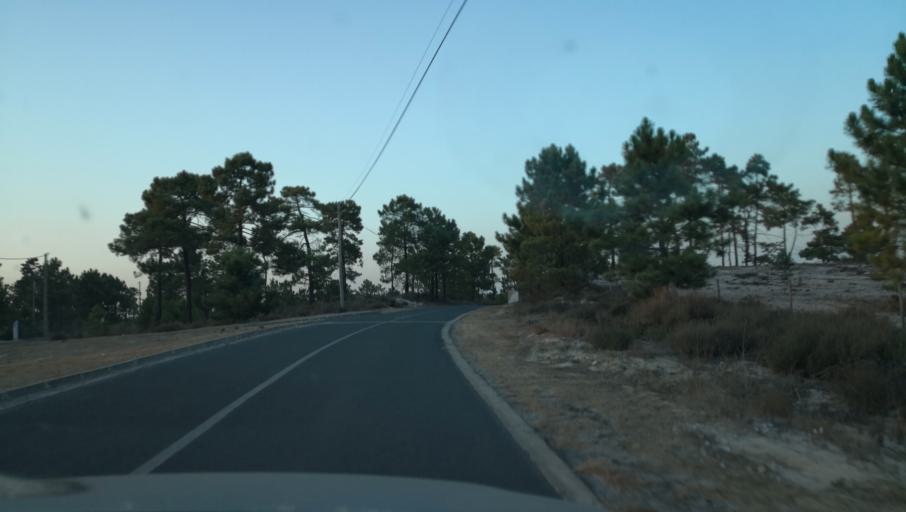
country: PT
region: Setubal
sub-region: Setubal
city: Setubal
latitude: 38.3855
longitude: -8.7831
